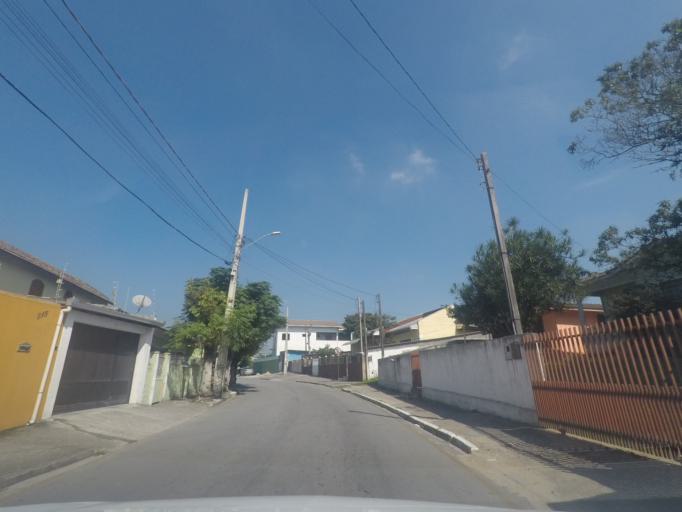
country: BR
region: Parana
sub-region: Paranagua
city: Paranagua
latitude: -25.5302
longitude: -48.5179
